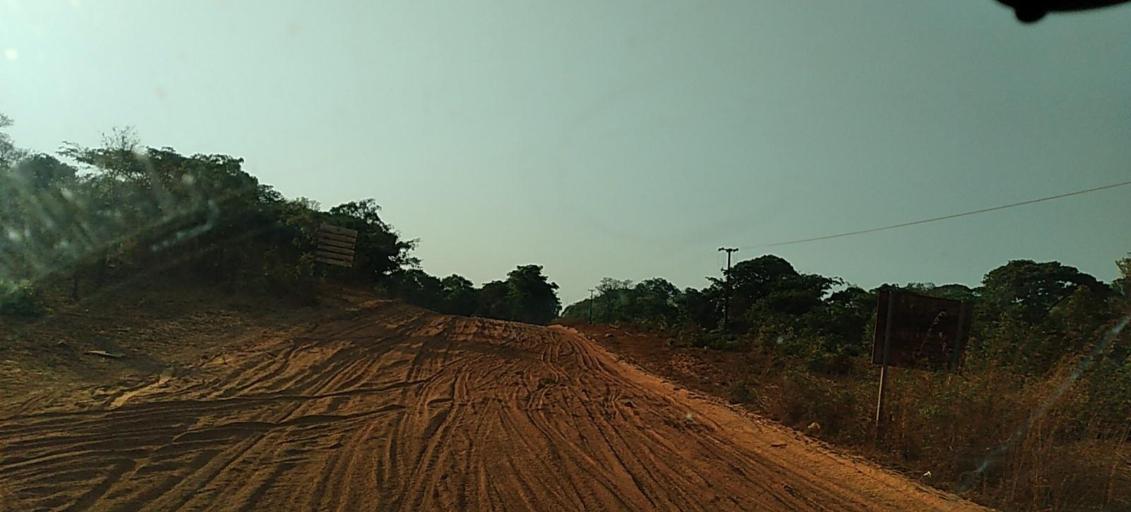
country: ZM
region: North-Western
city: Kasempa
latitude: -13.4711
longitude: 25.8652
